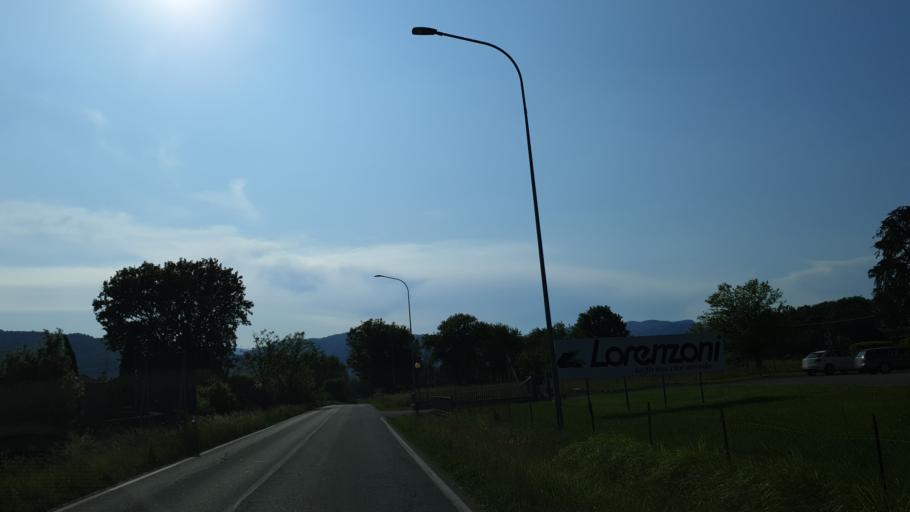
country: IT
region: Tuscany
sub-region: Province of Arezzo
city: Ponte a Poppi
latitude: 43.7378
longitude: 11.7512
